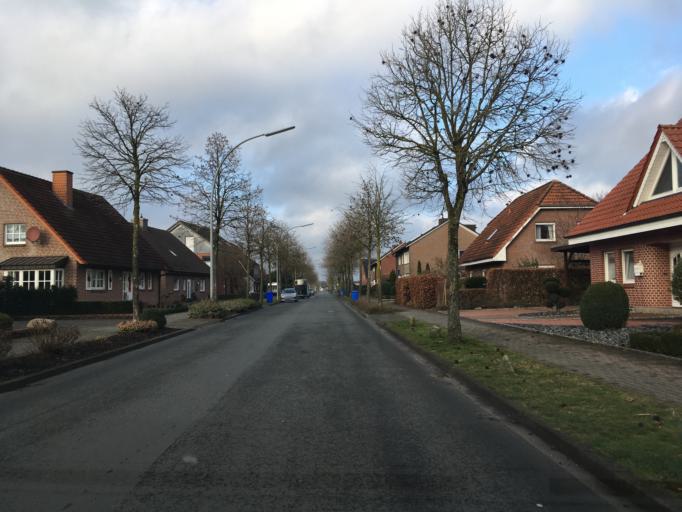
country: DE
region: North Rhine-Westphalia
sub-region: Regierungsbezirk Munster
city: Gescher
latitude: 51.9573
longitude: 6.9920
